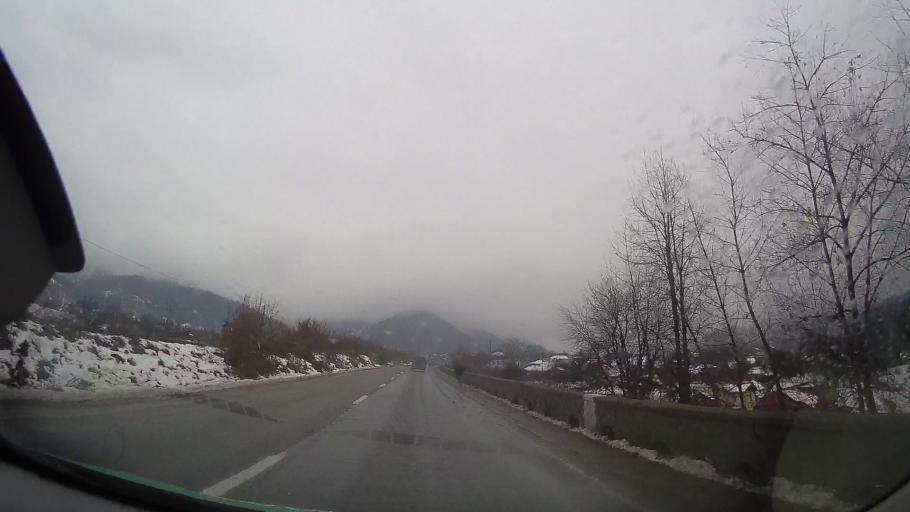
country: RO
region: Neamt
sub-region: Comuna Alexandru Cel Bun
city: Vadurele
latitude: 46.9380
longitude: 26.2626
